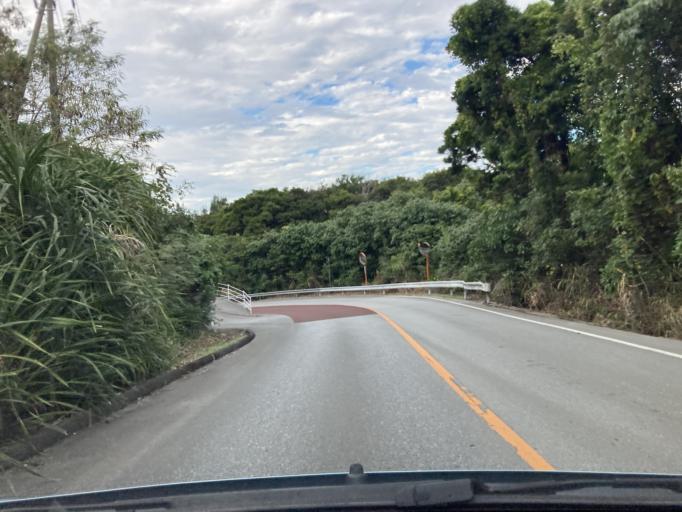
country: JP
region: Okinawa
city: Ishikawa
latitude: 26.4374
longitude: 127.8054
